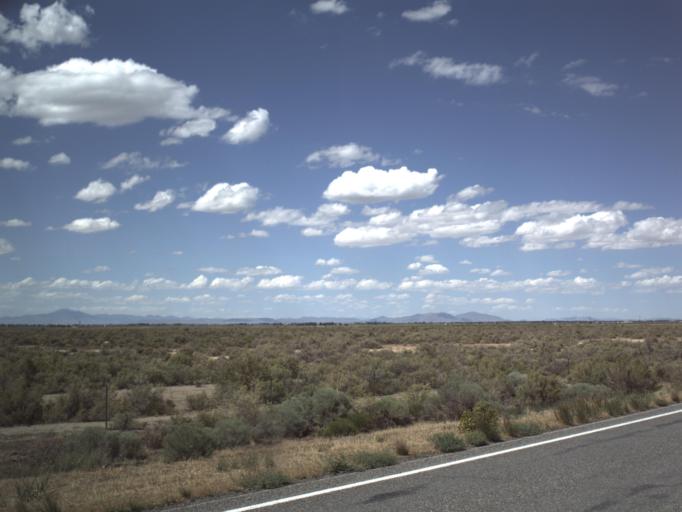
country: US
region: Utah
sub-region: Millard County
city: Delta
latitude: 39.2773
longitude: -112.4581
